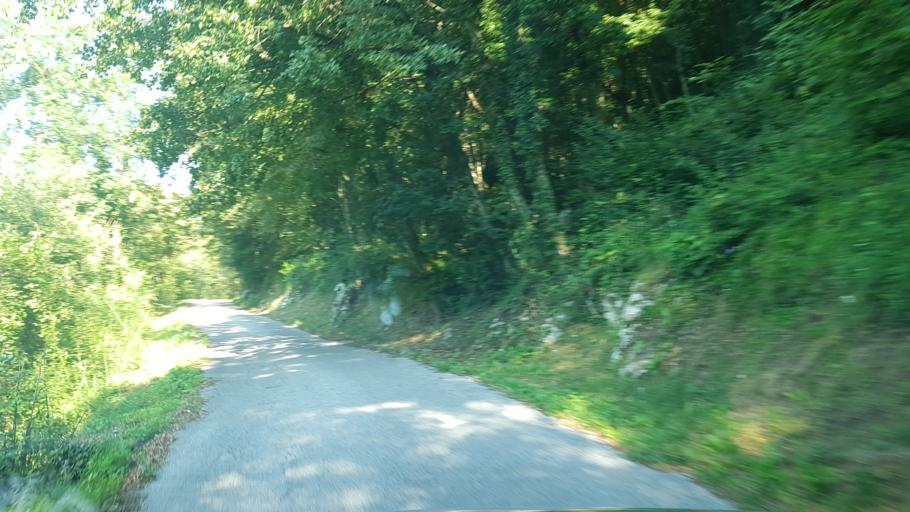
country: IT
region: Friuli Venezia Giulia
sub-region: Provincia di Udine
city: Nimis
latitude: 46.2324
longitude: 13.2461
